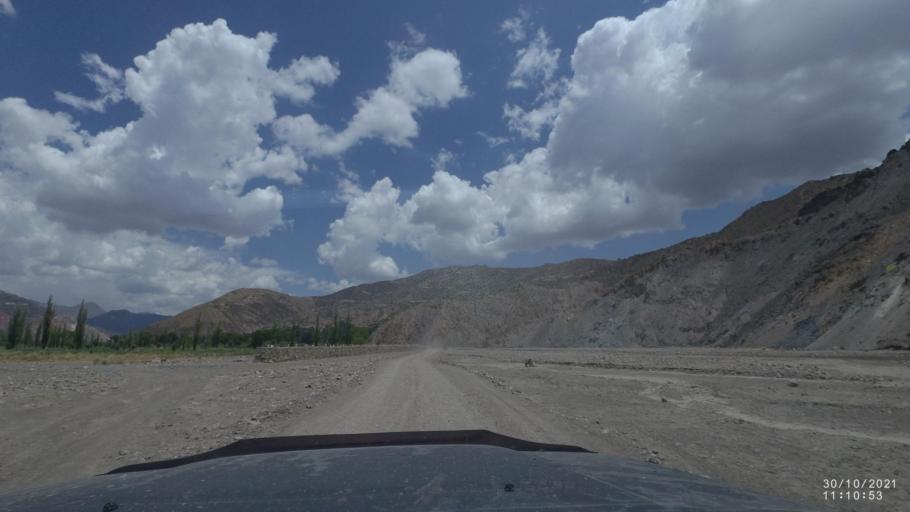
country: BO
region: Cochabamba
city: Sipe Sipe
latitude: -17.5260
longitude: -66.5616
